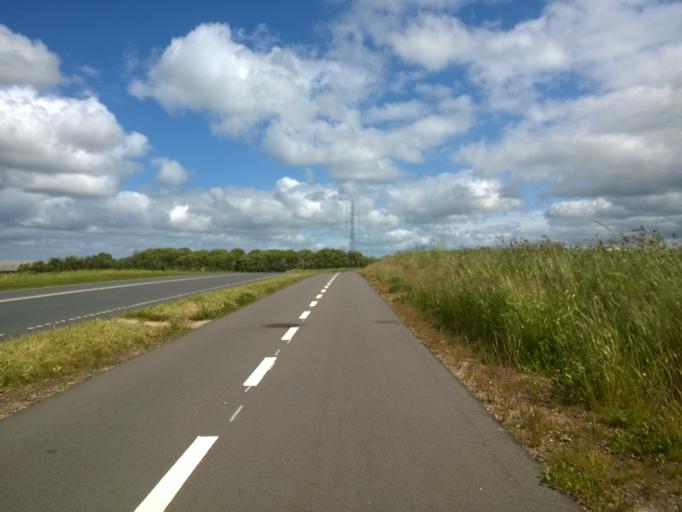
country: DK
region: Central Jutland
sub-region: Holstebro Kommune
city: Vinderup
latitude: 56.4620
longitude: 8.8508
